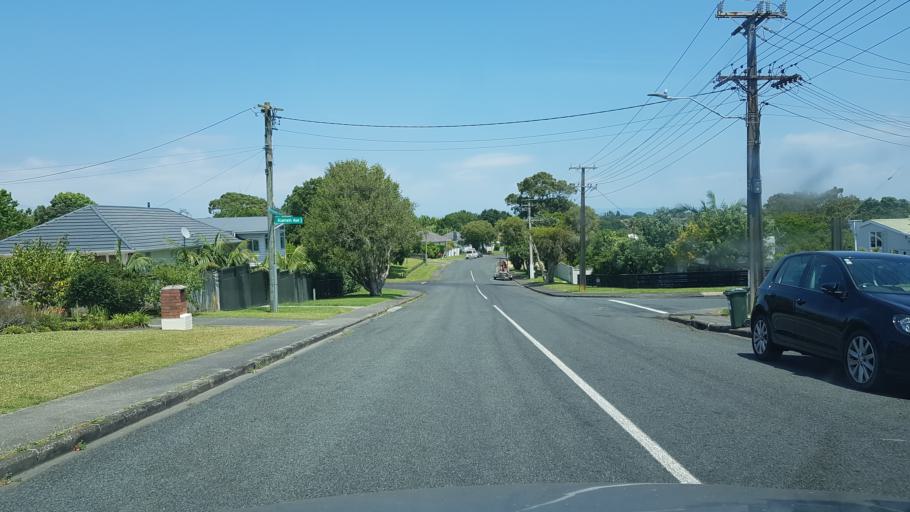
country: NZ
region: Auckland
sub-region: Auckland
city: North Shore
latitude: -36.8088
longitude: 174.7950
